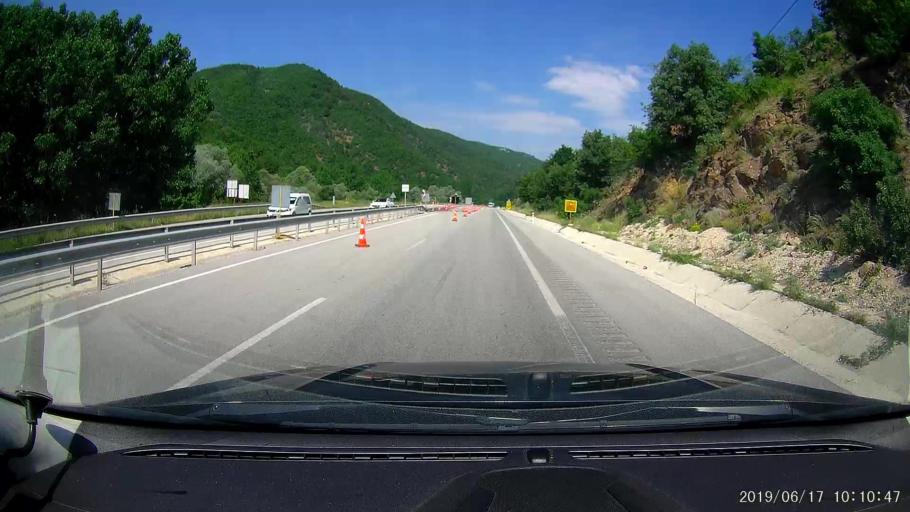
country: TR
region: Amasya
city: Saraycik
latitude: 40.9653
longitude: 35.0948
